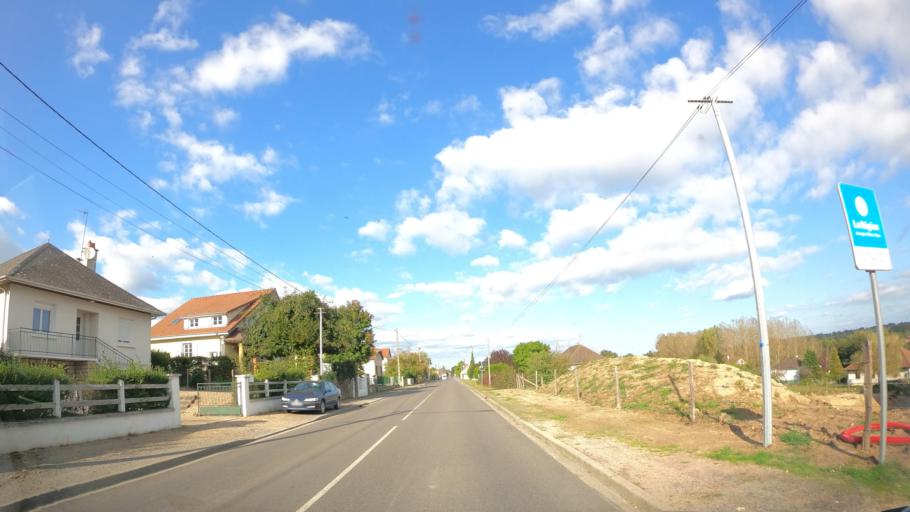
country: FR
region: Auvergne
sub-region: Departement de l'Allier
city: Dompierre-sur-Besbre
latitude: 46.5117
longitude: 3.6746
